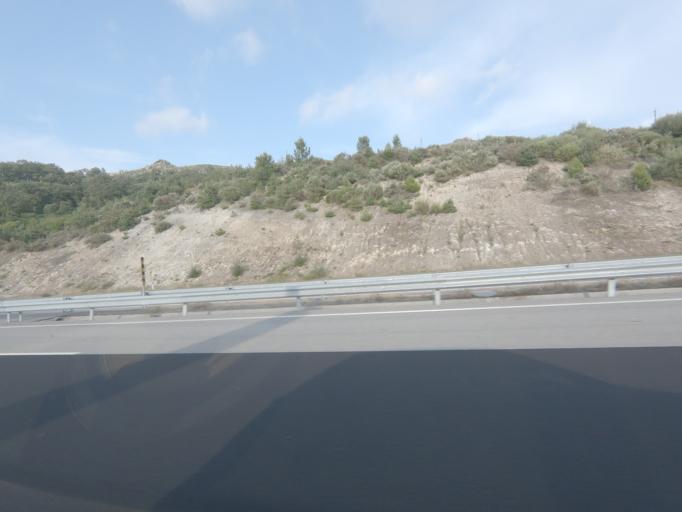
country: PT
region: Vila Real
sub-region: Vila Pouca de Aguiar
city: Vila Pouca de Aguiar
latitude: 41.4703
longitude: -7.6445
